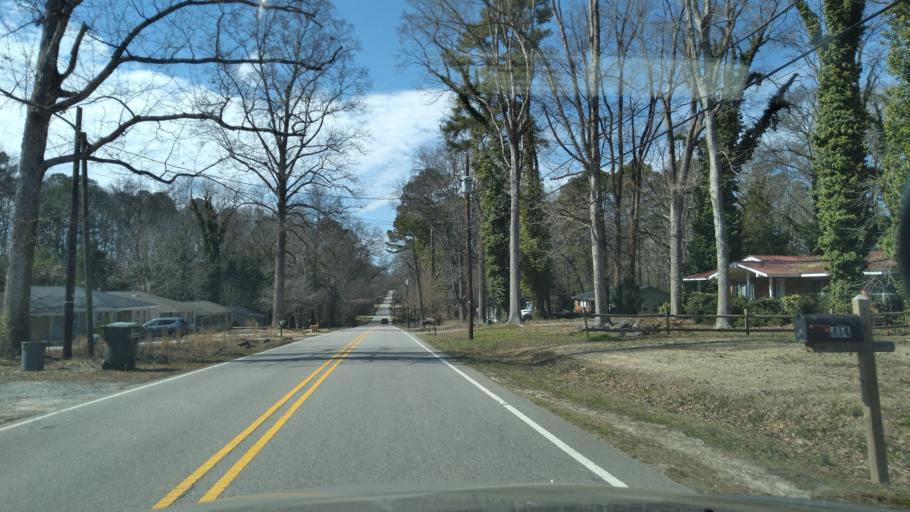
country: US
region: North Carolina
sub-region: Wake County
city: Garner
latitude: 35.7097
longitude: -78.6459
